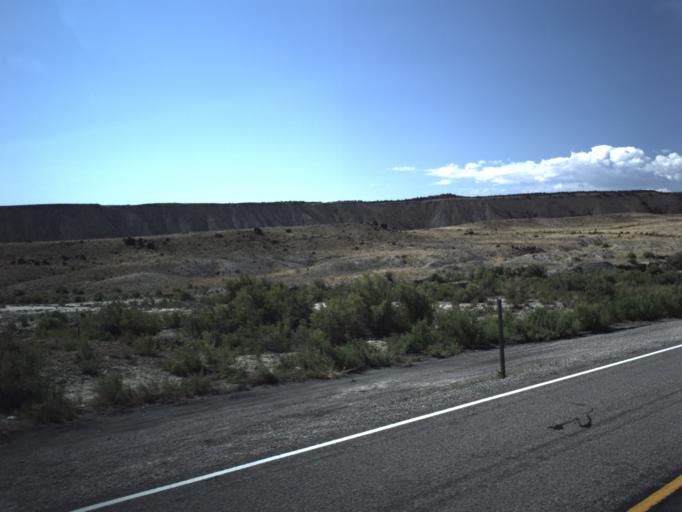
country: US
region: Utah
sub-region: Emery County
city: Ferron
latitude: 38.8042
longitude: -111.3392
